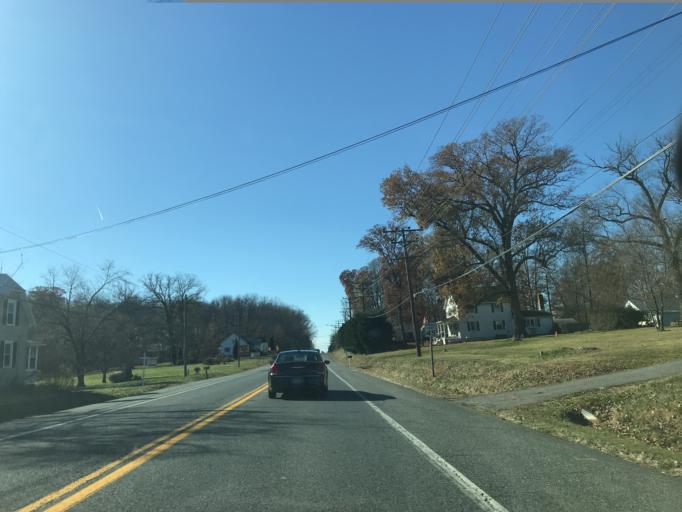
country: US
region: Maryland
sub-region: Harford County
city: South Bel Air
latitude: 39.5505
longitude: -76.2984
